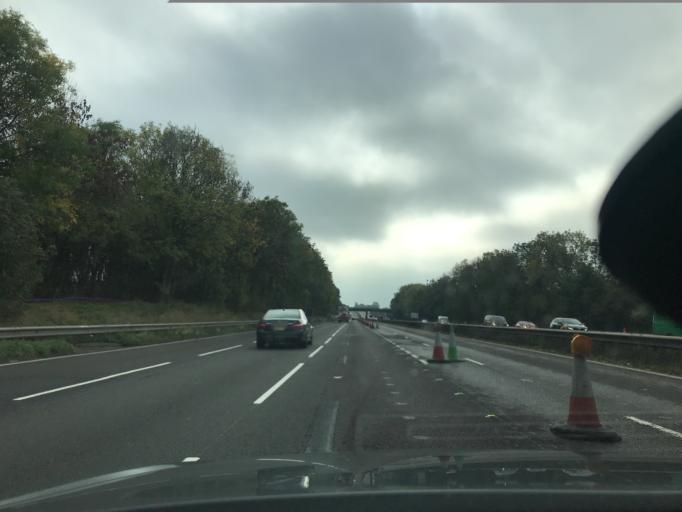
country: GB
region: England
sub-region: Staffordshire
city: Stone
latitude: 52.8547
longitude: -2.1612
